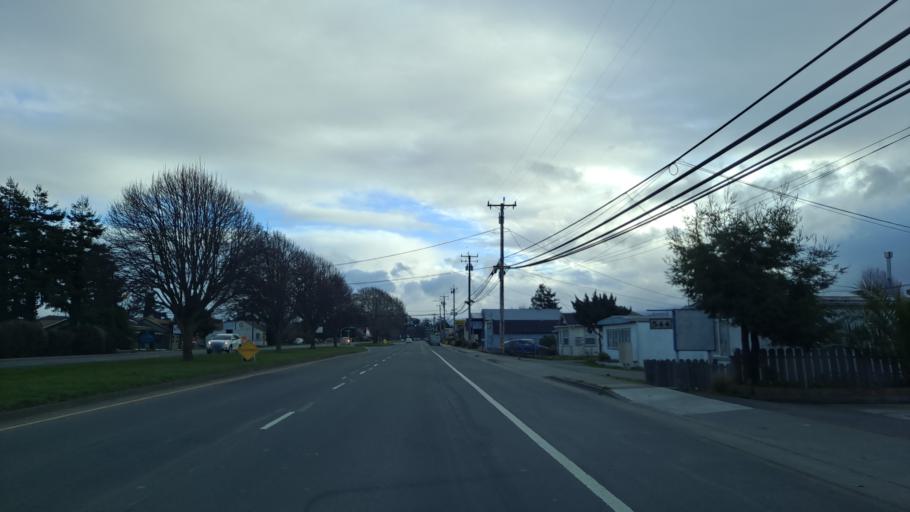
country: US
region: California
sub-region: Humboldt County
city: Fortuna
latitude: 40.5870
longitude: -124.1469
